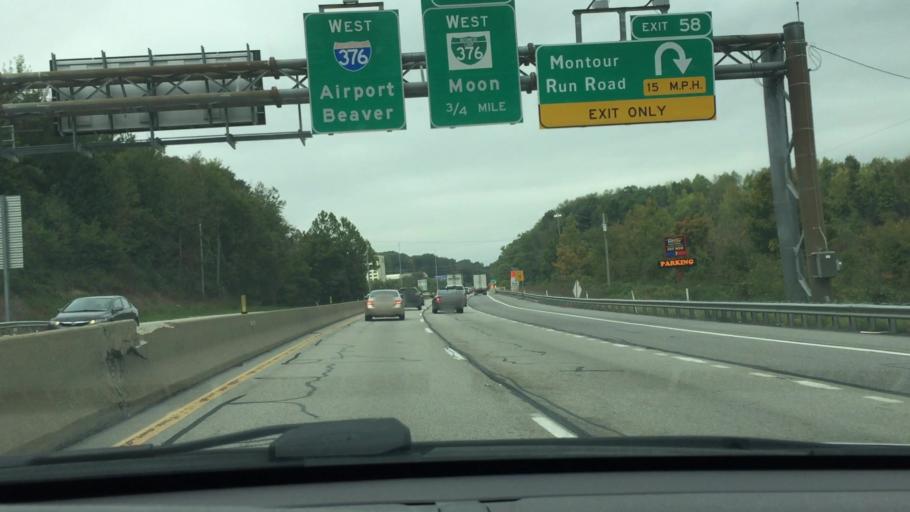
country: US
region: Pennsylvania
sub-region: Allegheny County
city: Enlow
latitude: 40.4563
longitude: -80.1862
